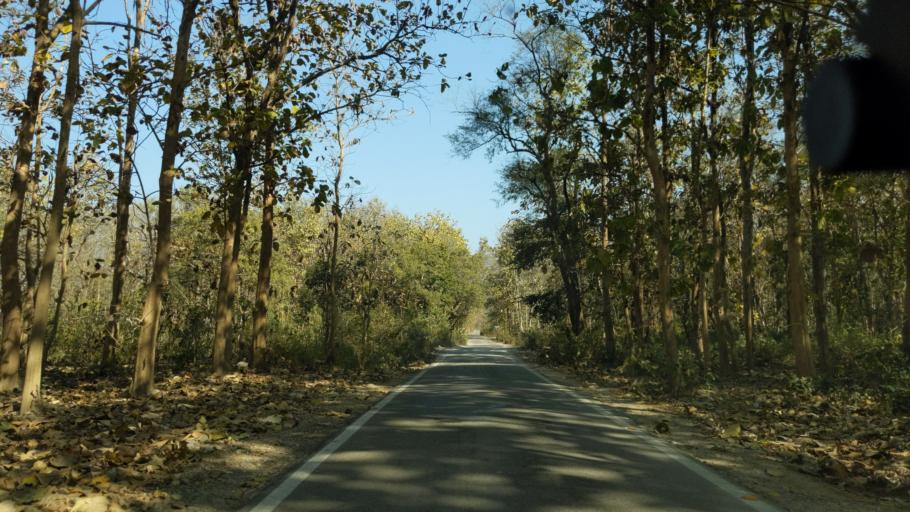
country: IN
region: Uttarakhand
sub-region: Naini Tal
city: Ramnagar
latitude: 29.4327
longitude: 79.1413
